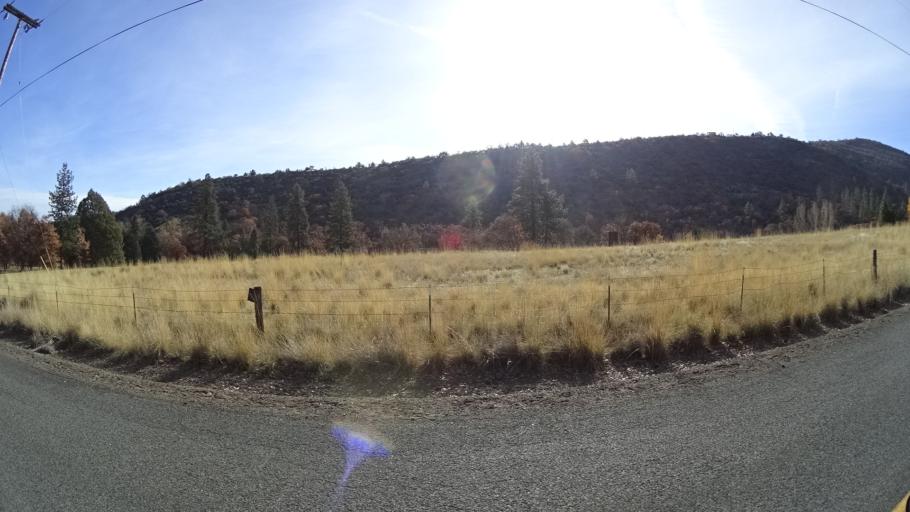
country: US
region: California
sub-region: Siskiyou County
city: Montague
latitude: 41.6330
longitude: -122.5787
